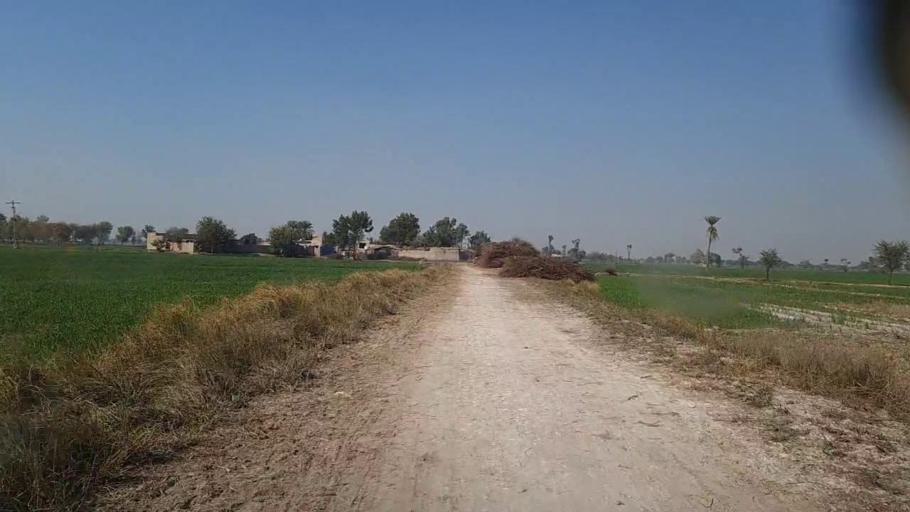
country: PK
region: Sindh
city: Khairpur
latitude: 28.0233
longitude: 69.7394
